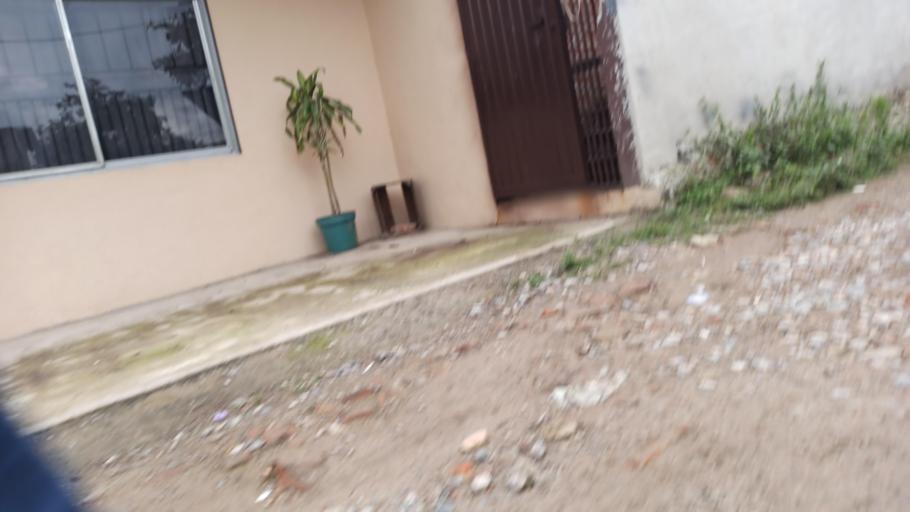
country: MX
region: Veracruz
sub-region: Papantla
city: El Chote
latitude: 20.3996
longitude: -97.3372
